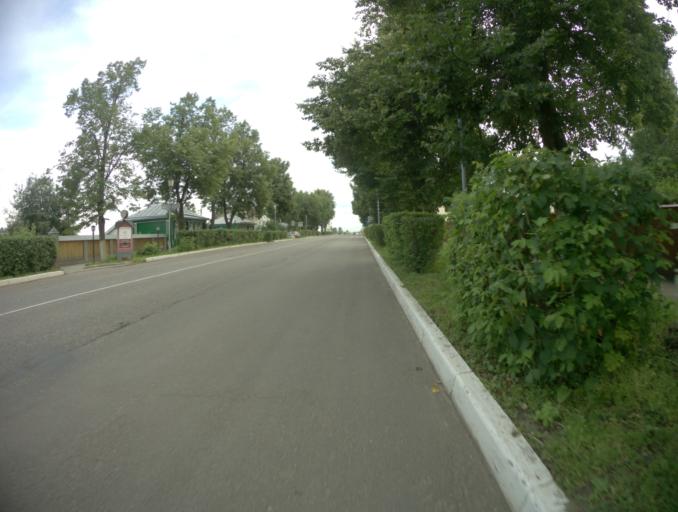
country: RU
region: Vladimir
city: Suzdal'
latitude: 56.4081
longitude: 40.4461
